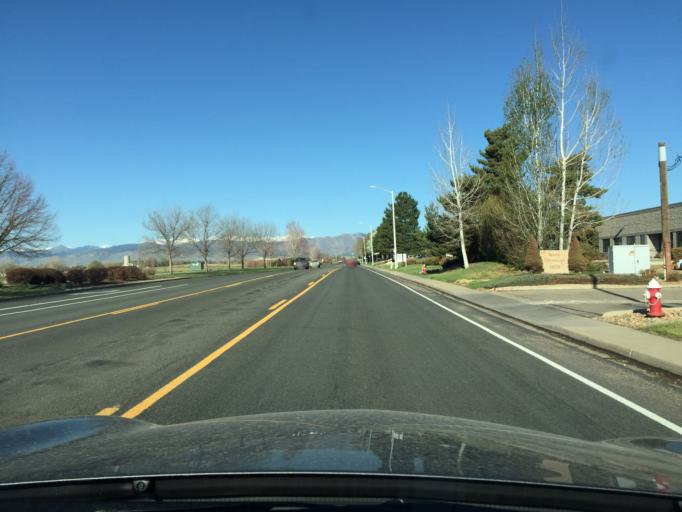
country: US
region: Colorado
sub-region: Boulder County
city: Longmont
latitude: 40.1380
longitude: -105.1254
